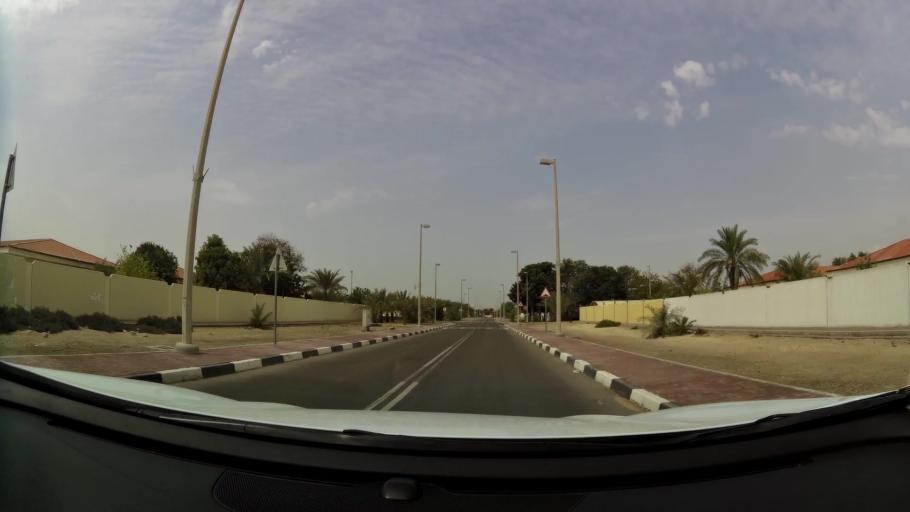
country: AE
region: Abu Dhabi
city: Abu Dhabi
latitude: 24.5196
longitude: 54.6859
